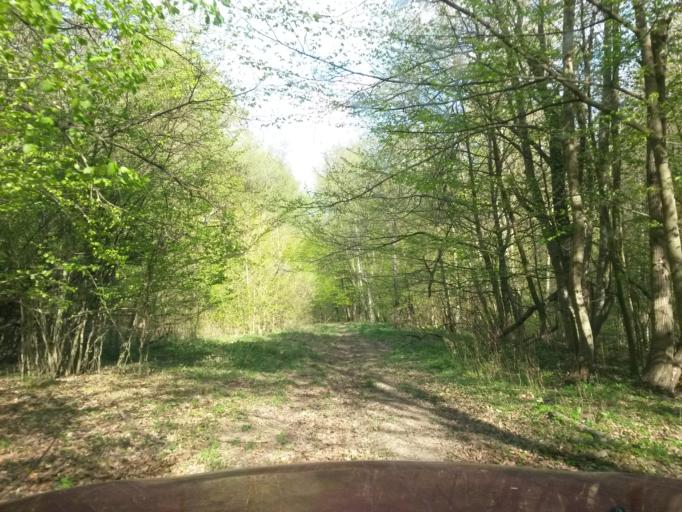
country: SK
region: Presovsky
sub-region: Okres Presov
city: Presov
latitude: 48.9469
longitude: 21.1373
